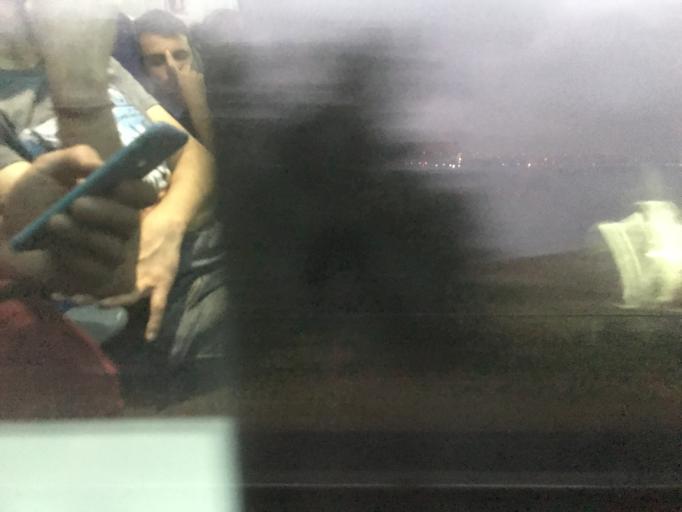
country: TR
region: Kocaeli
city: Derince
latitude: 40.7491
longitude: 29.8030
